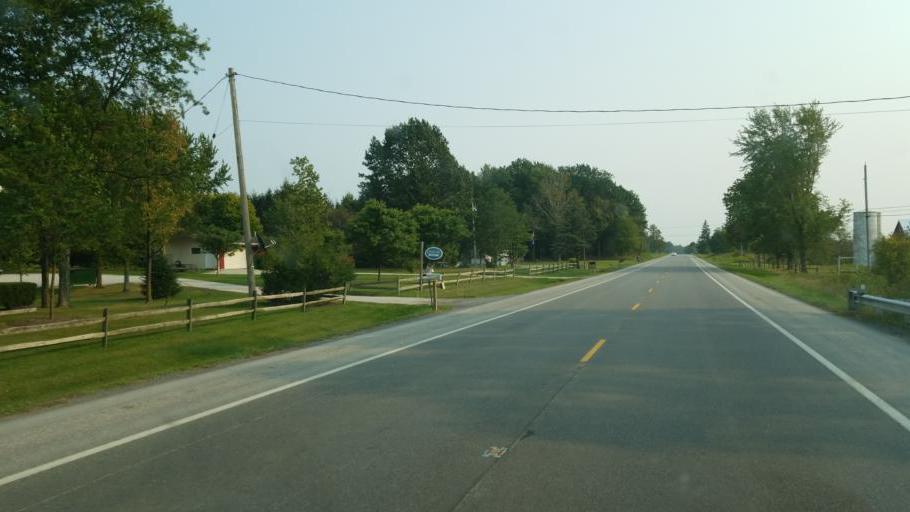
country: US
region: Ohio
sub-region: Geauga County
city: Middlefield
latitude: 41.4054
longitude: -81.0603
